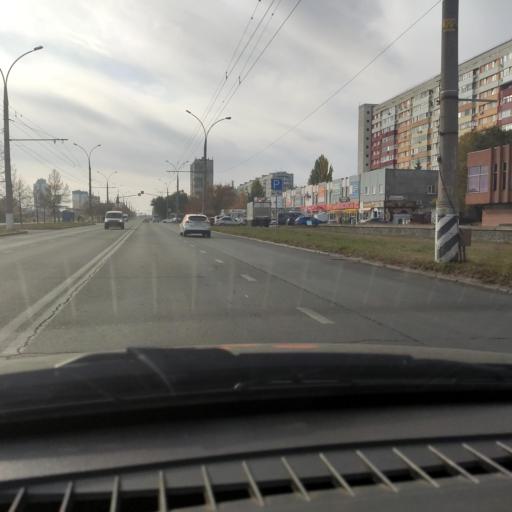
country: RU
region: Samara
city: Tol'yatti
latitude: 53.5120
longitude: 49.2720
